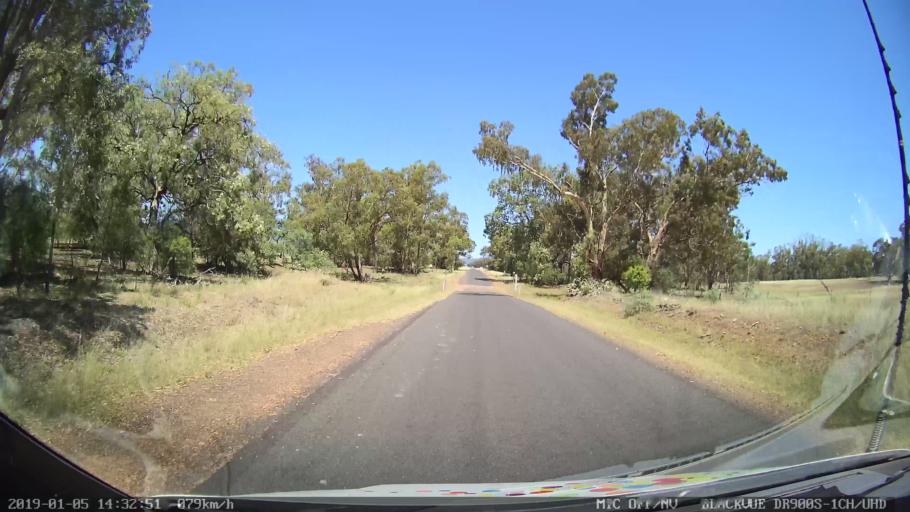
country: AU
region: New South Wales
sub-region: Tamworth Municipality
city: Phillip
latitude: -31.2225
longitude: 150.6234
